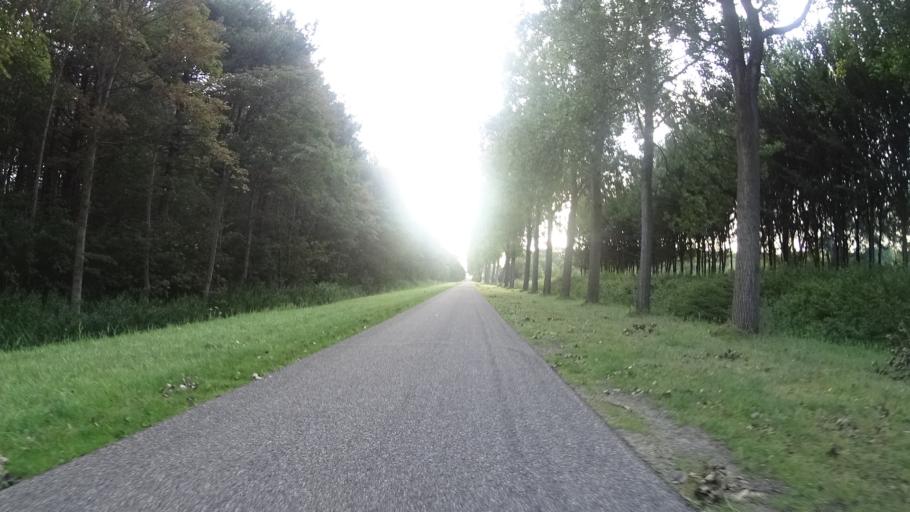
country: NL
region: North Holland
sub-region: Gemeente Hollands Kroon
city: Den Oever
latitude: 52.9030
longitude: 5.0468
